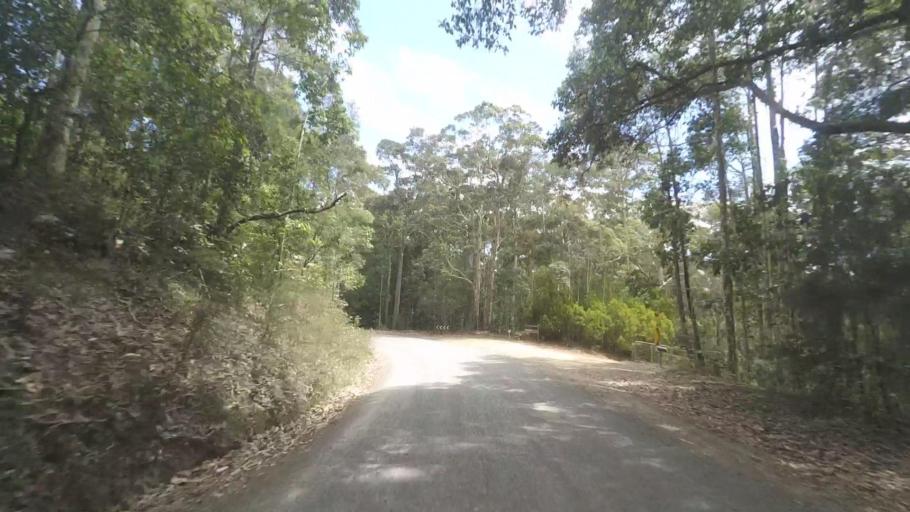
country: AU
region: New South Wales
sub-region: Shoalhaven Shire
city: Milton
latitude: -35.4358
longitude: 150.3311
